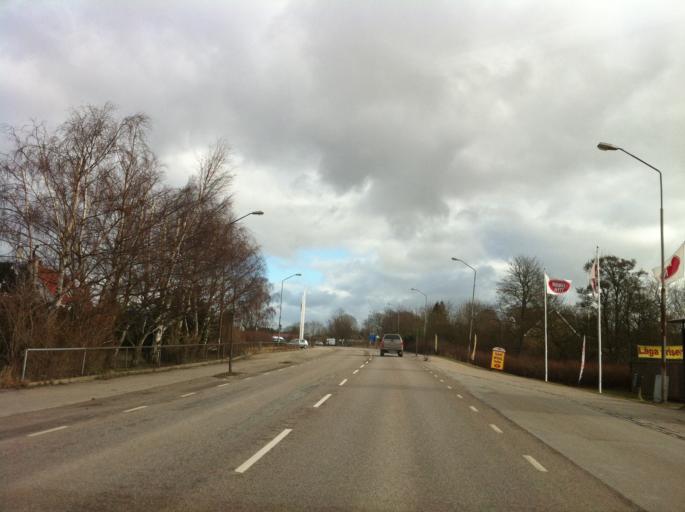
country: SE
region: Skane
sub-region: Bromolla Kommun
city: Bromoella
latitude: 56.0457
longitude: 14.4335
